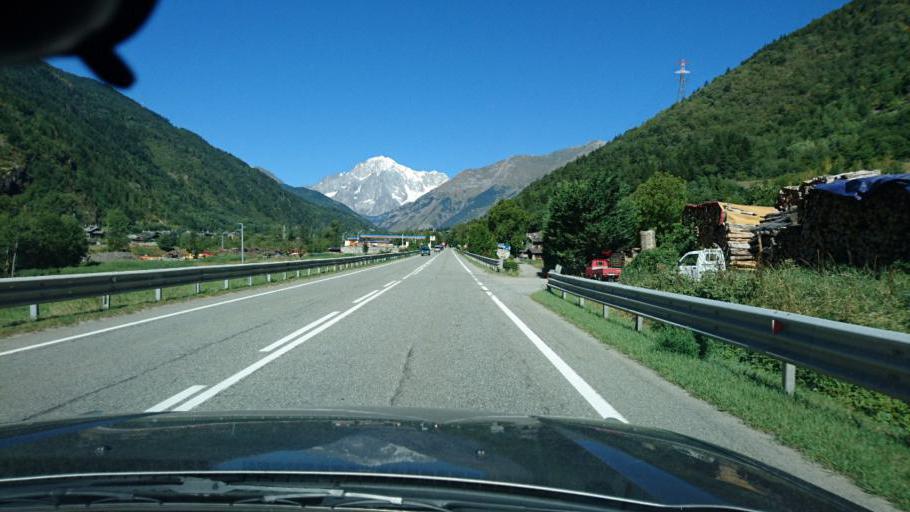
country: IT
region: Aosta Valley
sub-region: Valle d'Aosta
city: La Salle
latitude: 45.7230
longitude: 7.0990
